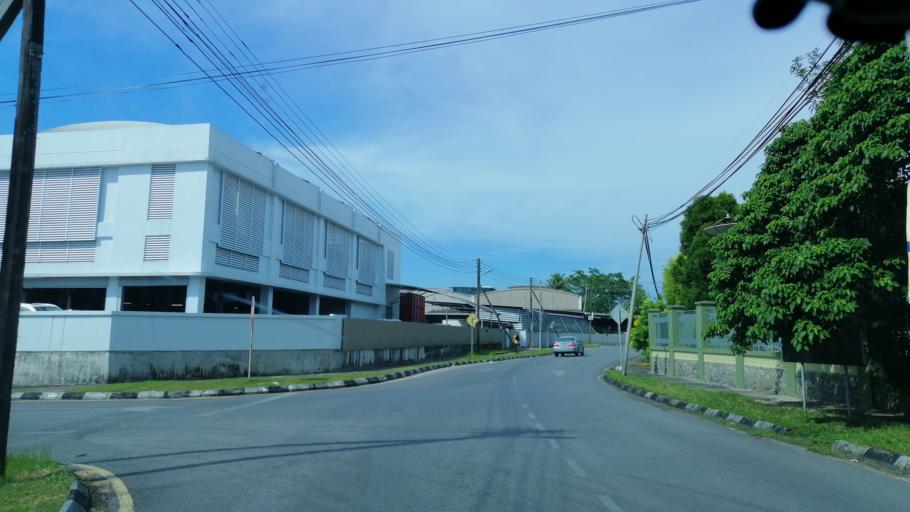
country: MY
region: Sarawak
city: Kuching
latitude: 1.5204
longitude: 110.3530
